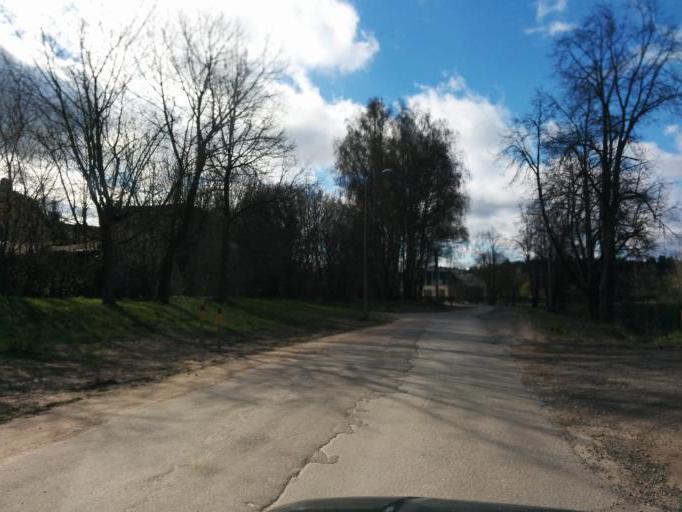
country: LV
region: Kekava
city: Balozi
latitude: 56.8878
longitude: 24.1578
